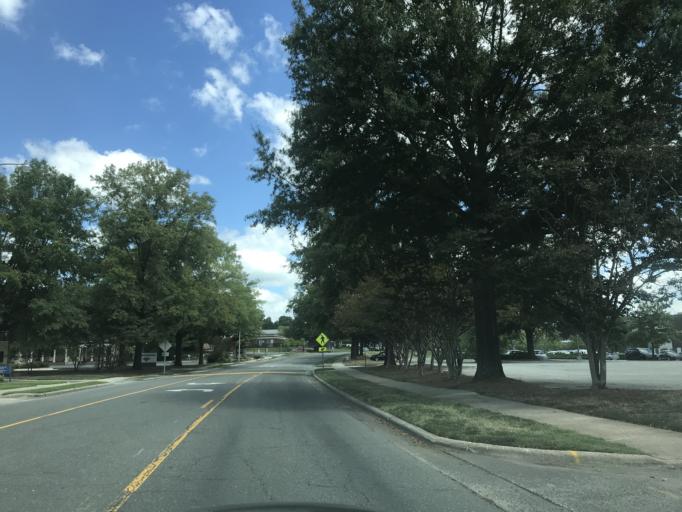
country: US
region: North Carolina
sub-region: Orange County
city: Chapel Hill
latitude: 35.9280
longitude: -79.0300
